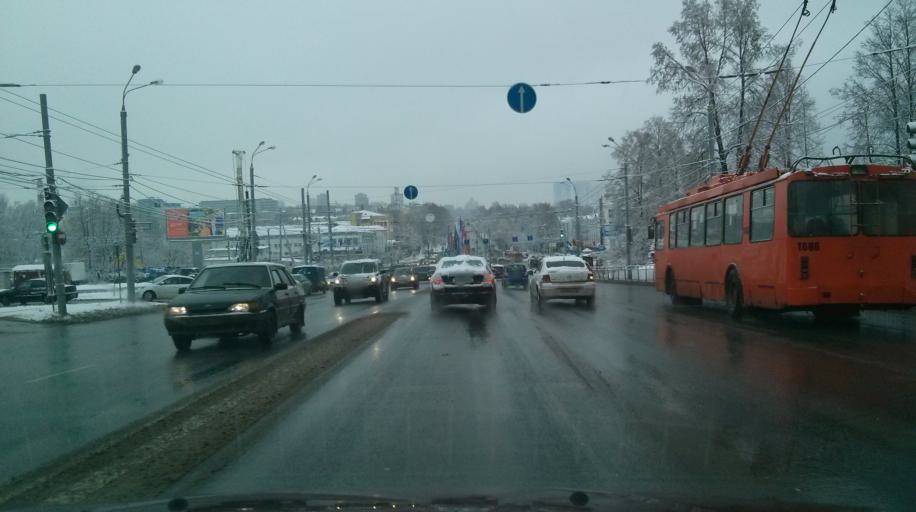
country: RU
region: Nizjnij Novgorod
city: Nizhniy Novgorod
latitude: 56.2573
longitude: 43.9713
